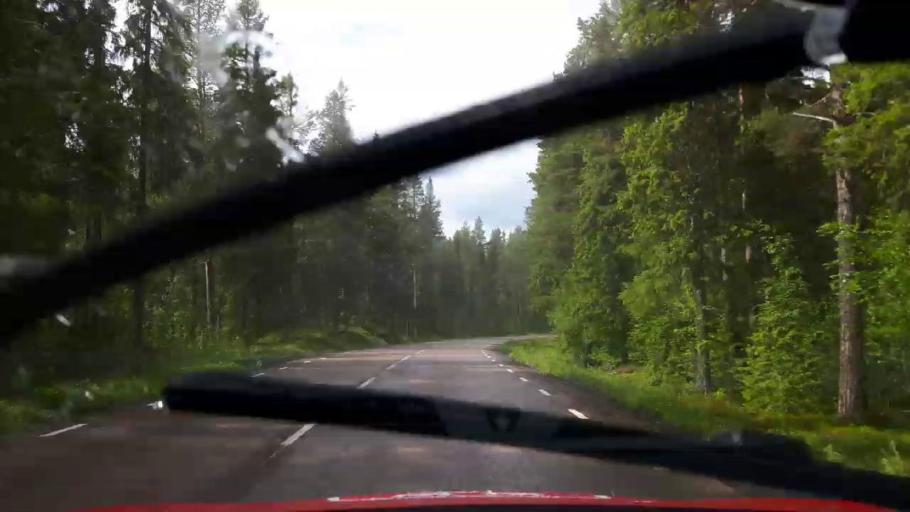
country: SE
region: Jaemtland
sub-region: Krokoms Kommun
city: Valla
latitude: 63.9603
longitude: 14.1847
